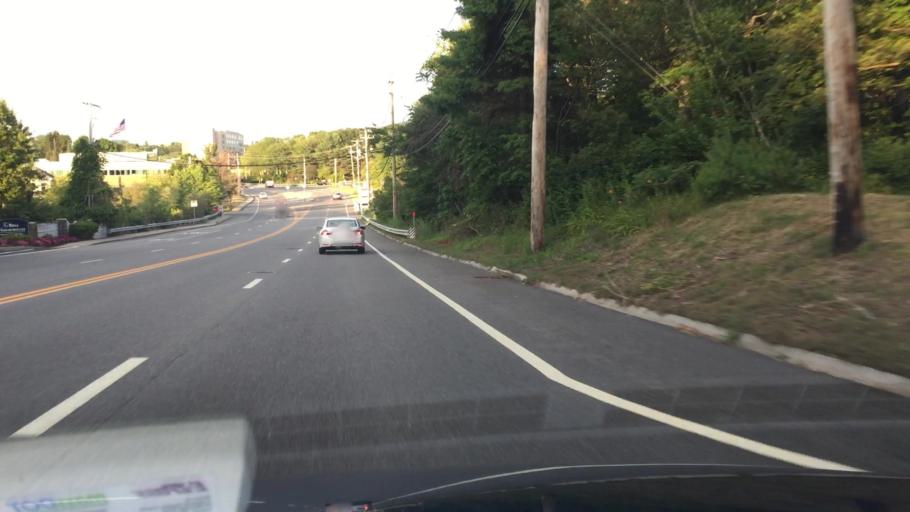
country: US
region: Massachusetts
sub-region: Worcester County
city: Northborough
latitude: 42.3359
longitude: -71.5982
